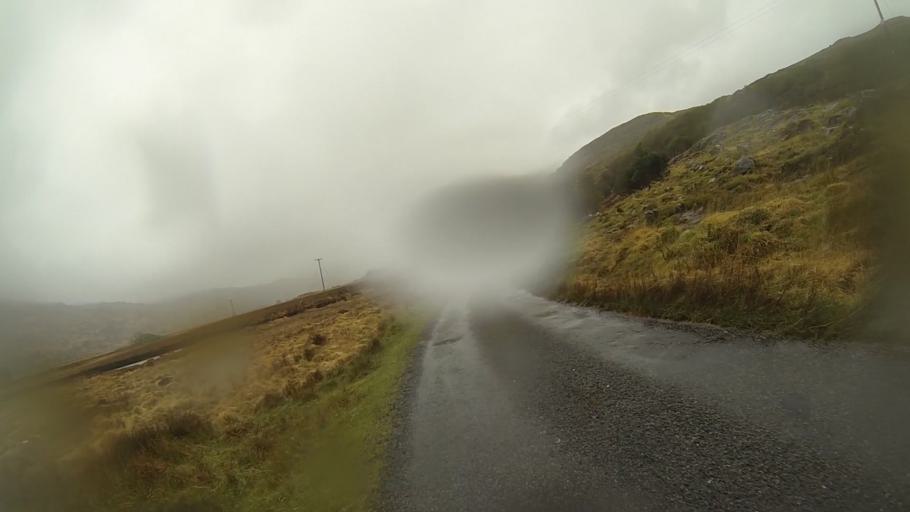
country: IE
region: Munster
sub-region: Ciarrai
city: Kenmare
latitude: 51.9540
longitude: -9.6391
